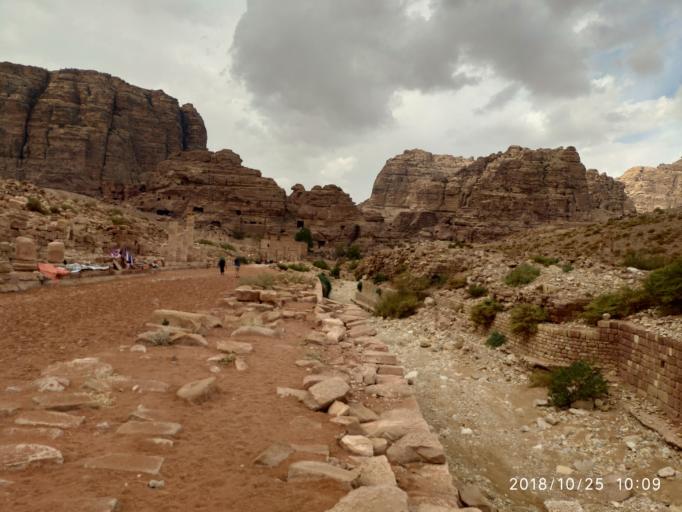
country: JO
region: Ma'an
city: Petra
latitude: 30.3290
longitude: 35.4446
